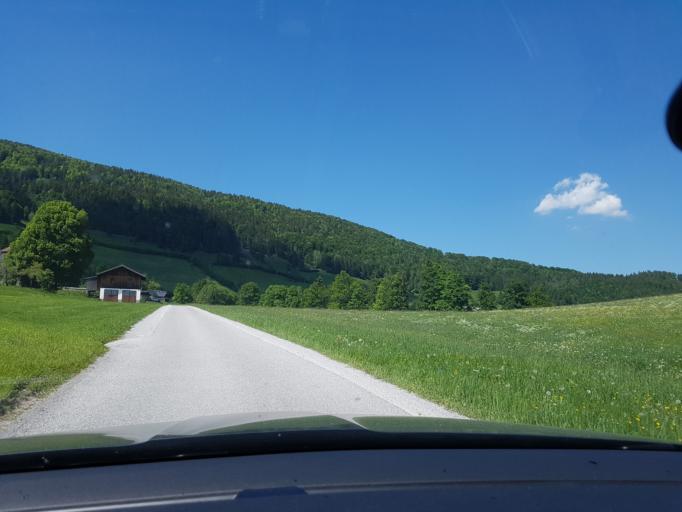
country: AT
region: Salzburg
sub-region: Politischer Bezirk Salzburg-Umgebung
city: Koppl
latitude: 47.7905
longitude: 13.1259
